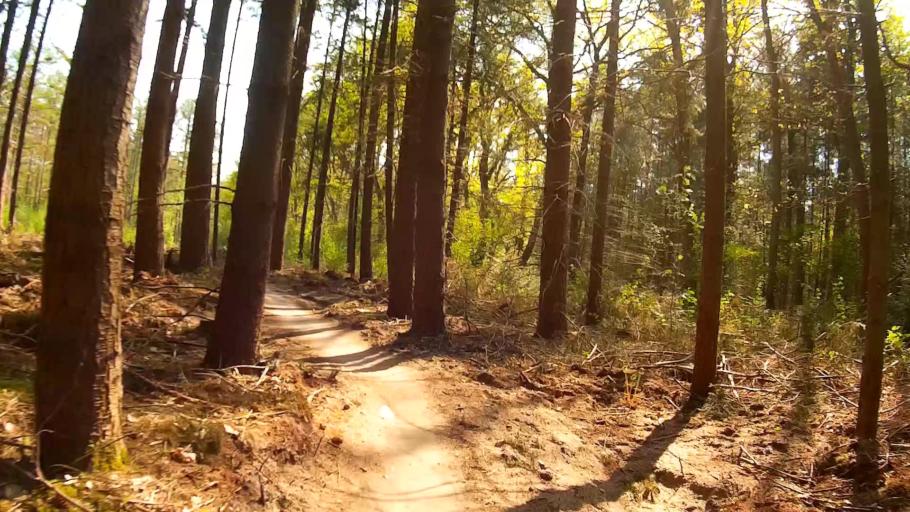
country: NL
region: Utrecht
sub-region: Gemeente Baarn
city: Baarn
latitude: 52.1953
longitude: 5.2336
